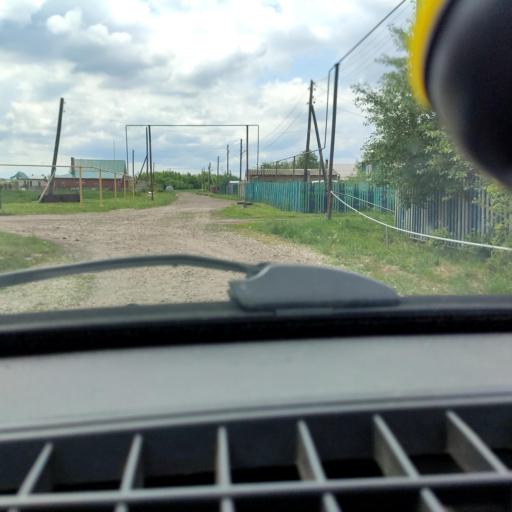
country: RU
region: Samara
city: Povolzhskiy
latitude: 53.6482
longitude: 49.6960
